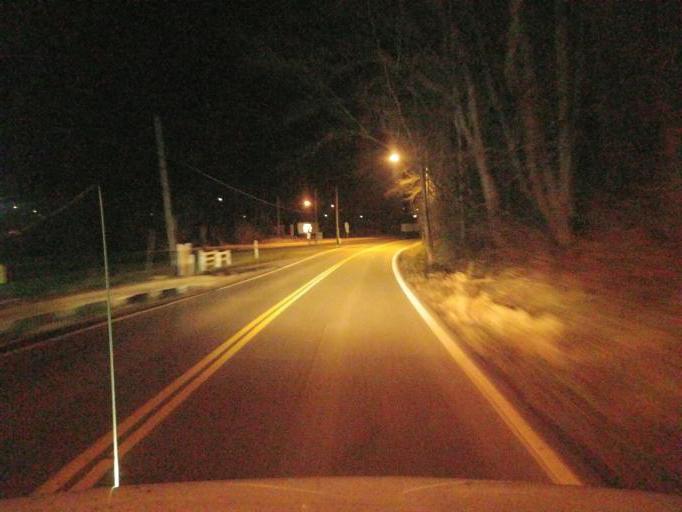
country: US
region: Ohio
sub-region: Harrison County
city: Cadiz
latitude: 40.3949
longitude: -81.0821
